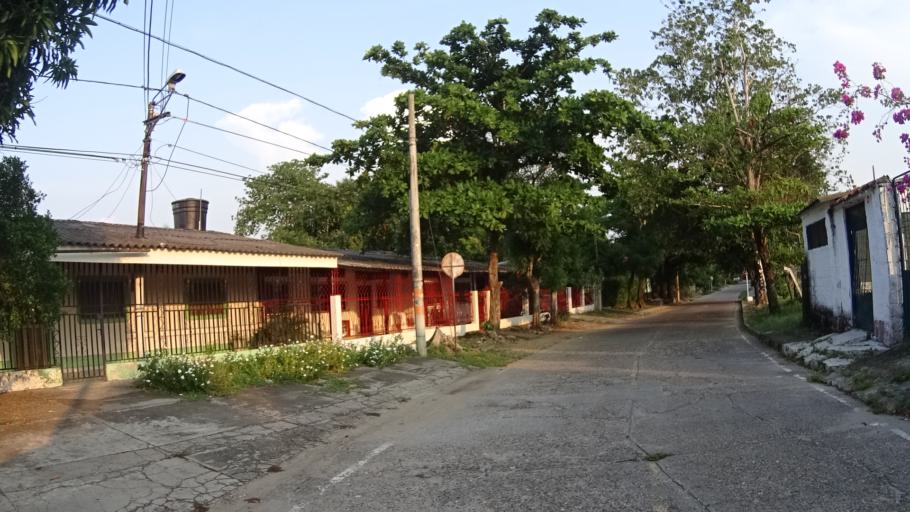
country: CO
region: Cundinamarca
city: Puerto Salgar
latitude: 5.4798
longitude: -74.6690
